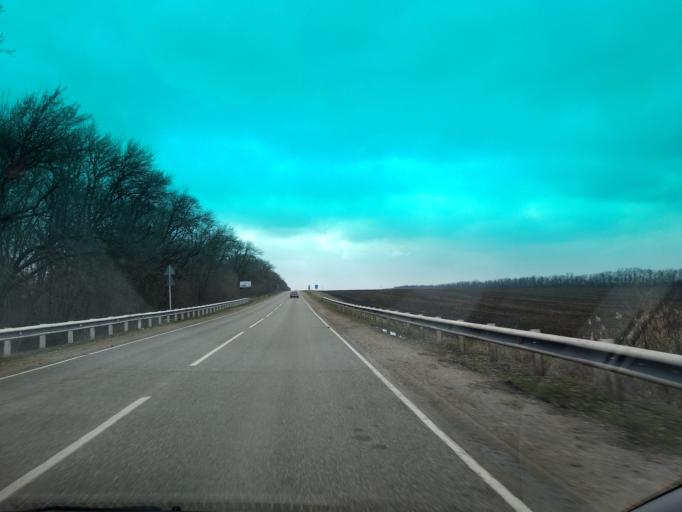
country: RU
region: Krasnodarskiy
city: Novorozhdestvenskaya
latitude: 45.7528
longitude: 39.9223
